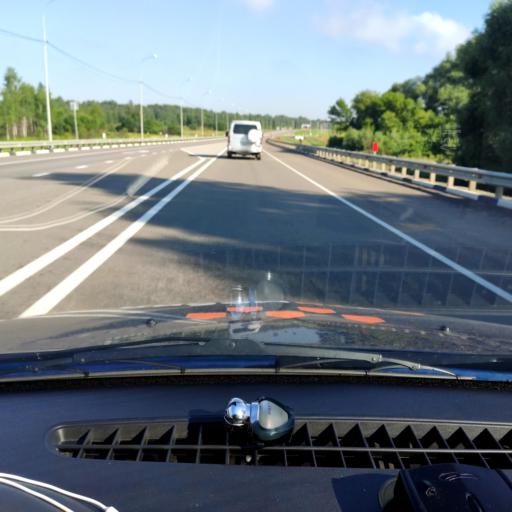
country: RU
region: Orjol
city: Orel
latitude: 52.8863
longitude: 36.1638
